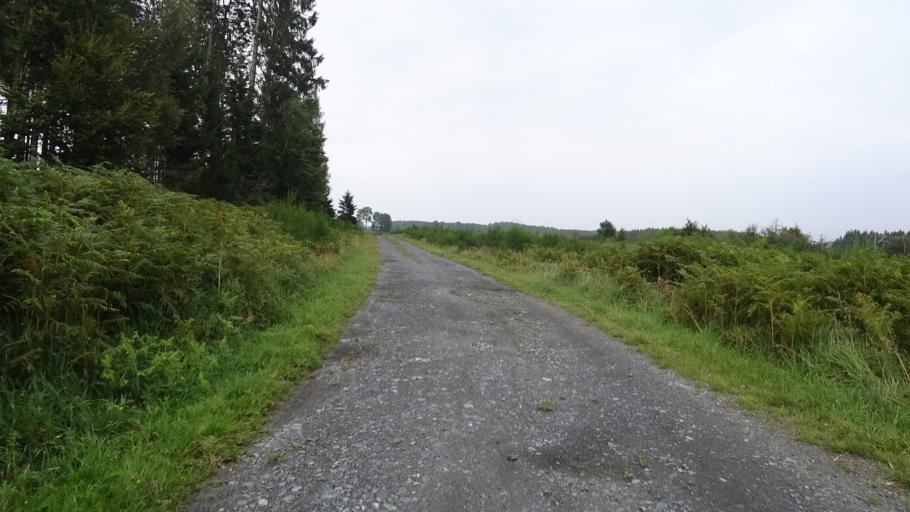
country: BE
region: Wallonia
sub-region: Province du Luxembourg
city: Chiny
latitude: 49.7906
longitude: 5.3259
